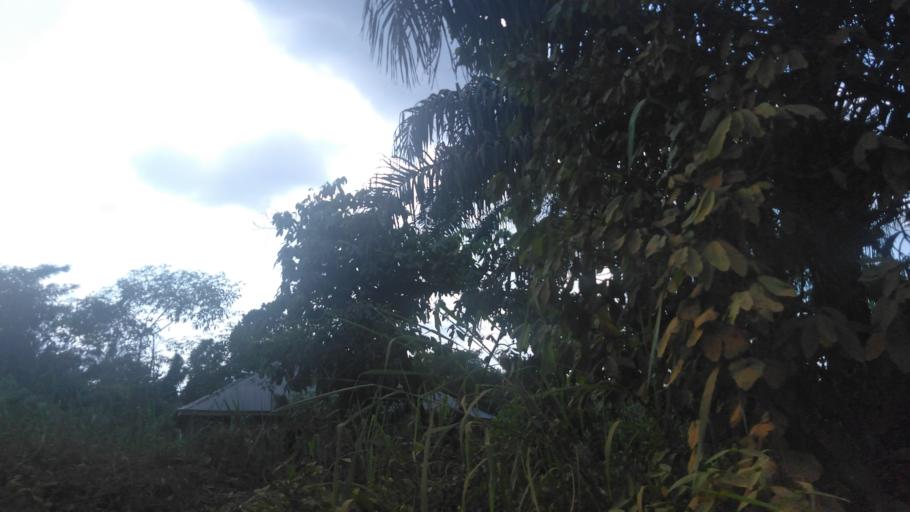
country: NG
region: Osun
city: Ifetedo
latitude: 7.0123
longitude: 4.6355
